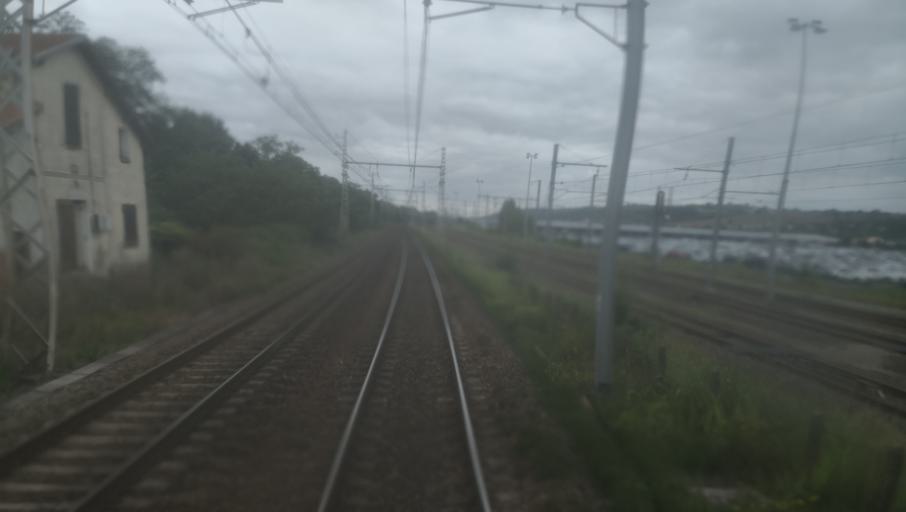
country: FR
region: Midi-Pyrenees
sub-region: Departement de la Haute-Garonne
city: Castelnau-d'Estretefonds
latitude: 43.7748
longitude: 1.3521
